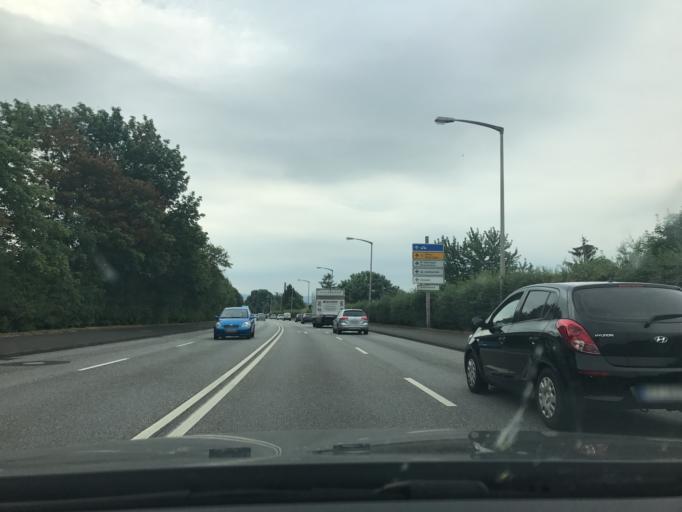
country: DE
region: Hesse
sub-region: Regierungsbezirk Kassel
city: Kassel
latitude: 51.3070
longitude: 9.5135
